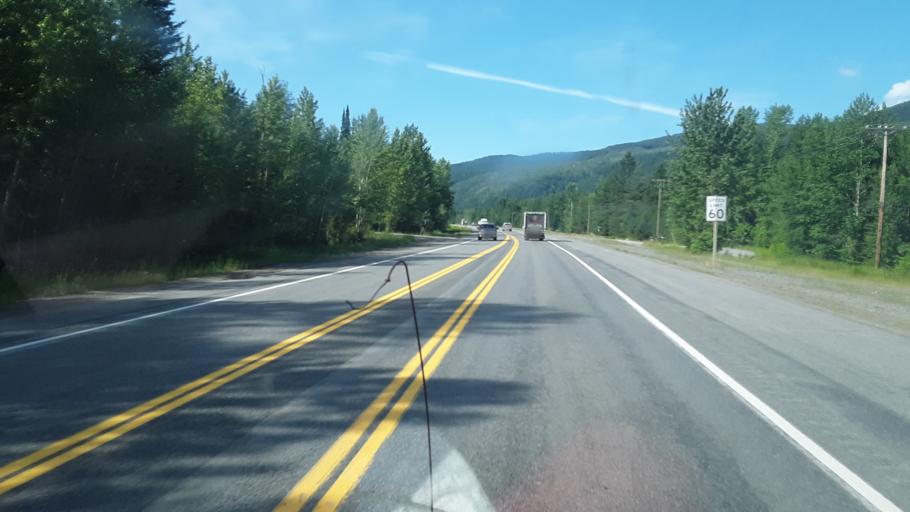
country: US
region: Idaho
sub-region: Bonner County
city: Ponderay
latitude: 48.3994
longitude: -116.5324
